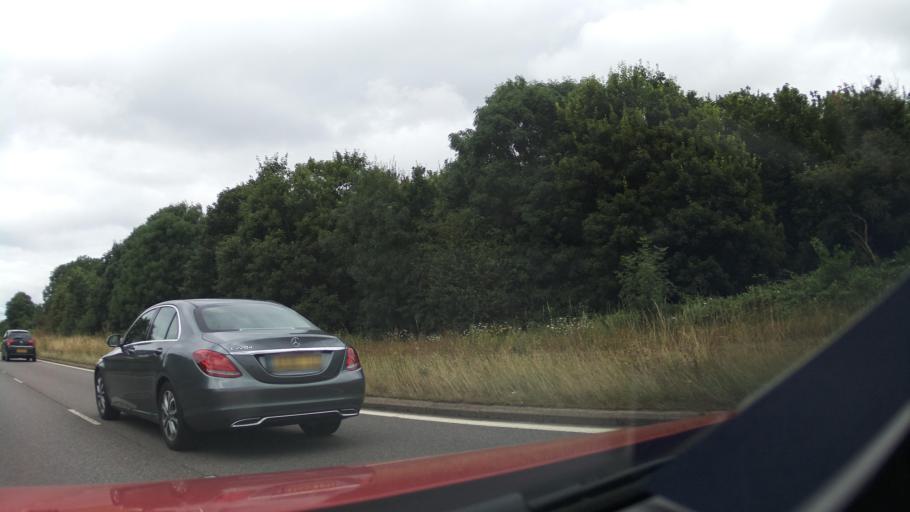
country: GB
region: England
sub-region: Northamptonshire
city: Kettering
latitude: 52.4290
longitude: -0.7322
